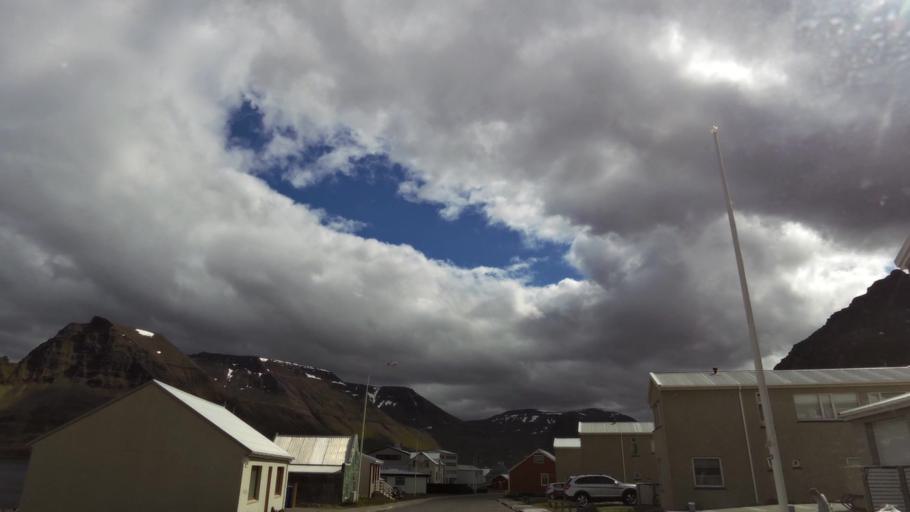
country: IS
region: Westfjords
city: Isafjoerdur
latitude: 66.1613
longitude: -23.2479
